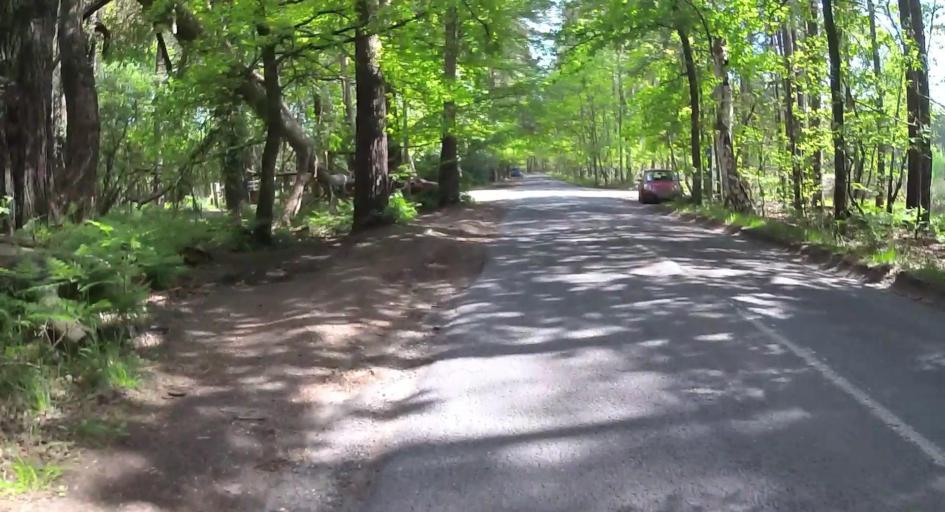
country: GB
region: England
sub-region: Surrey
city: Farnham
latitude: 51.1837
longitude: -0.7810
